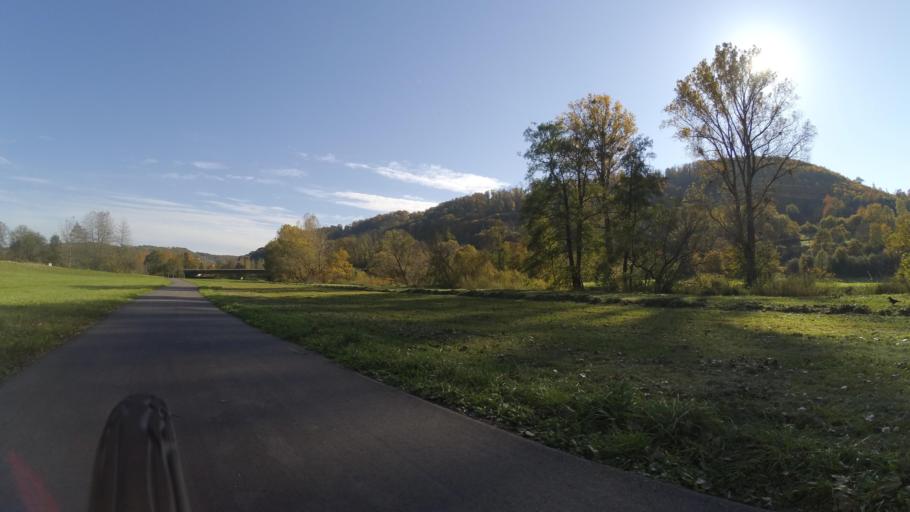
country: DE
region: Baden-Wuerttemberg
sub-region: Regierungsbezirk Stuttgart
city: Forchtenberg
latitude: 49.2921
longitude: 9.5465
